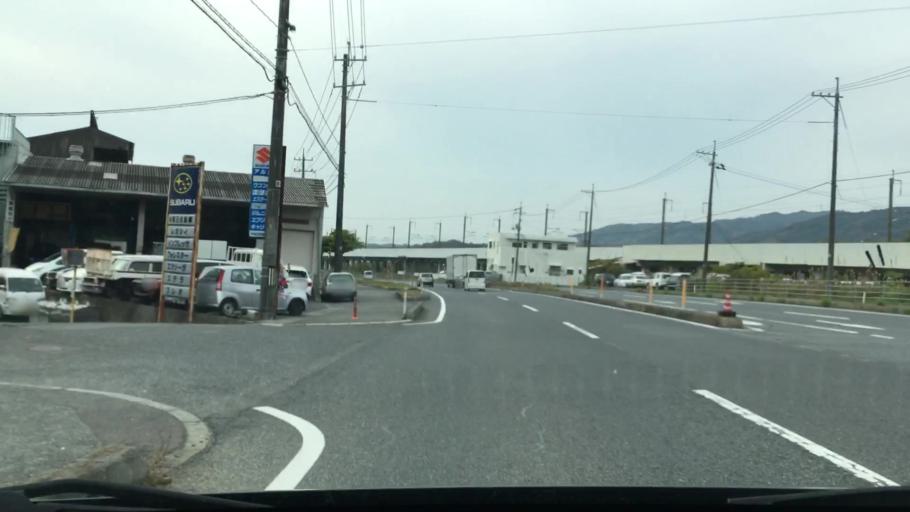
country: JP
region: Yamaguchi
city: Kudamatsu
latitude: 34.0350
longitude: 131.8922
